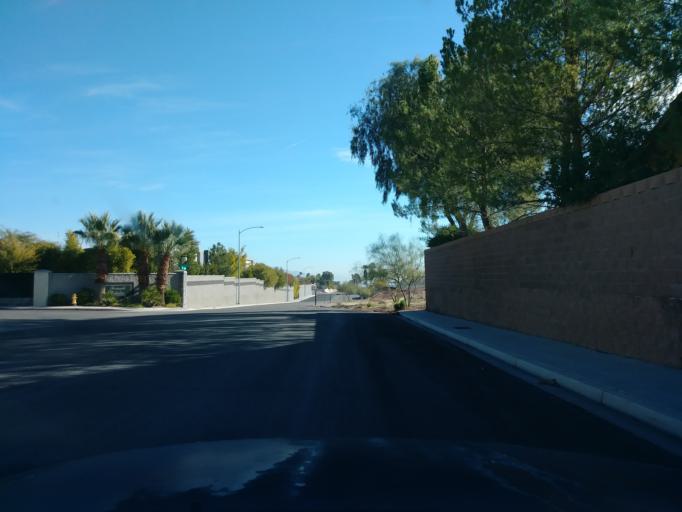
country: US
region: Nevada
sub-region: Clark County
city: Spring Valley
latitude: 36.1495
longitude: -115.2731
